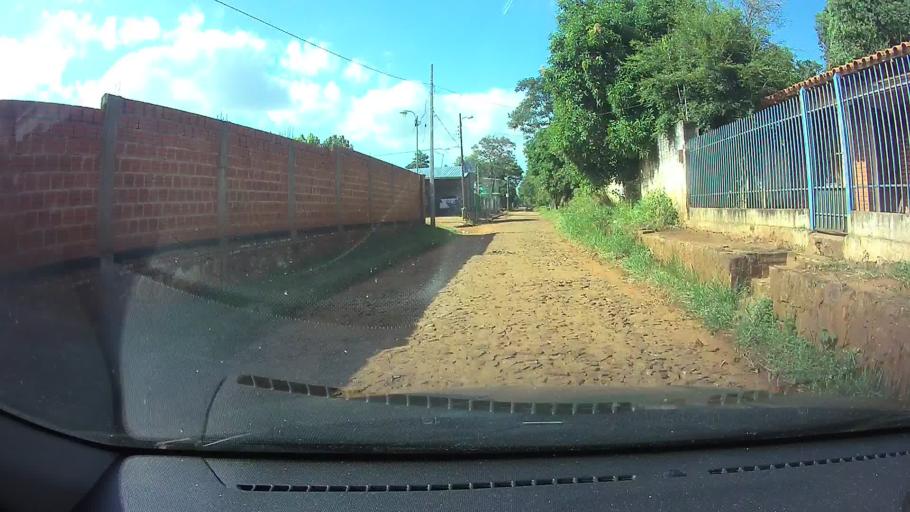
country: PY
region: Central
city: Limpio
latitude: -25.2467
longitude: -57.4679
